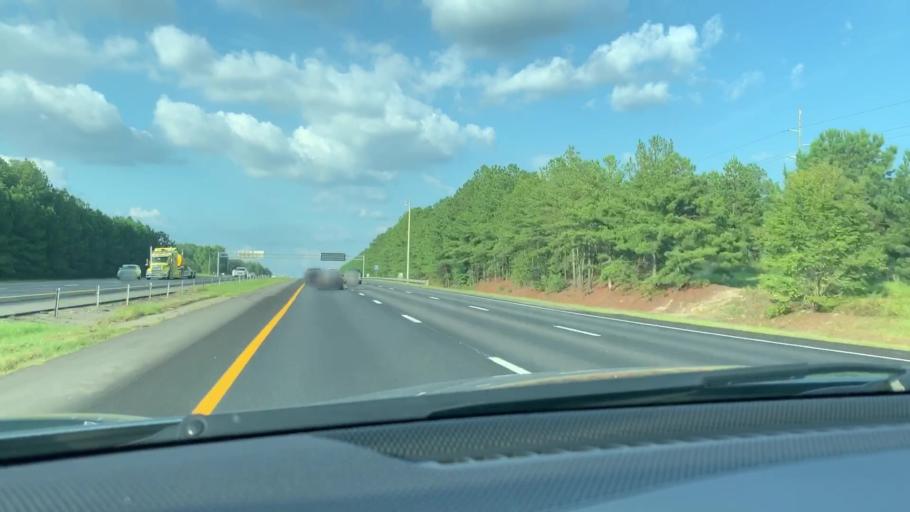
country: US
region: South Carolina
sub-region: Richland County
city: Woodfield
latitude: 34.0274
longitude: -80.9426
